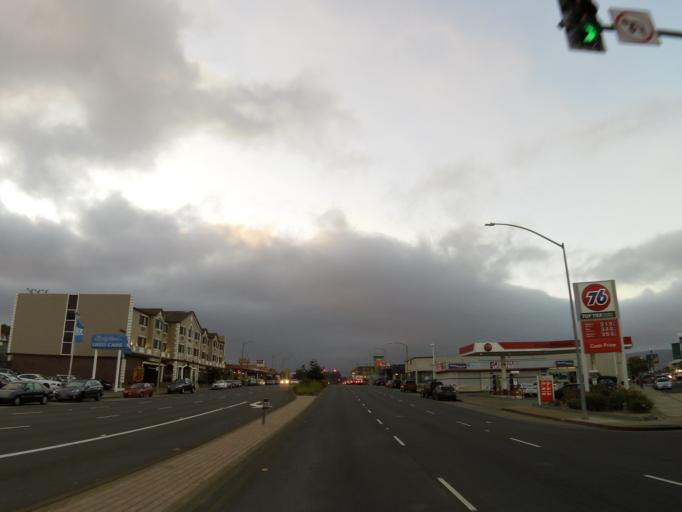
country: US
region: California
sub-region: San Mateo County
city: San Bruno
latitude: 37.6211
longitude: -122.4112
